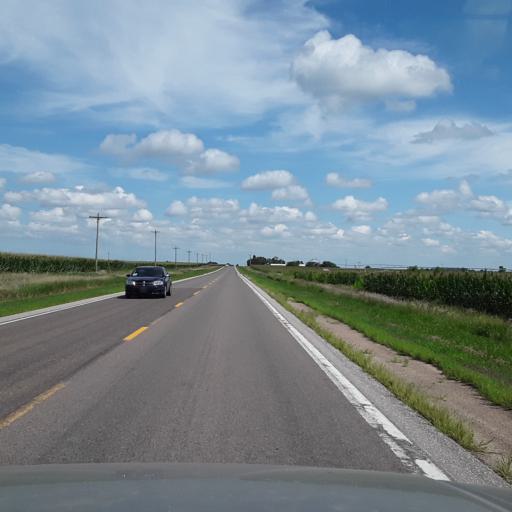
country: US
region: Nebraska
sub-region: Polk County
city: Osceola
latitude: 41.0560
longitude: -97.4064
